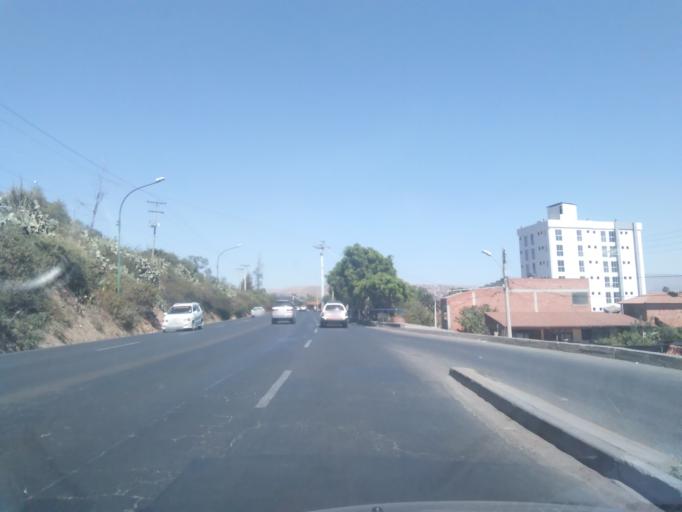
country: BO
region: Cochabamba
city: Cochabamba
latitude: -17.3865
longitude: -66.1411
